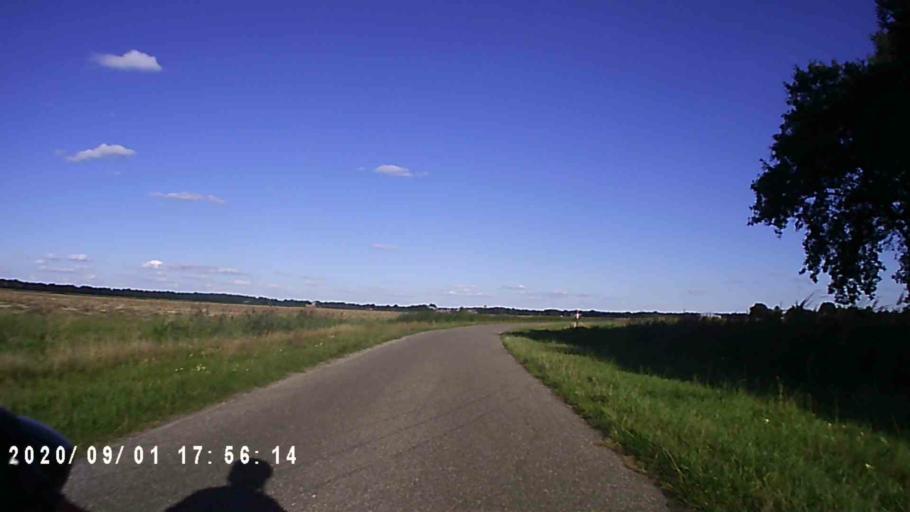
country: NL
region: Groningen
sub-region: Gemeente Slochteren
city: Slochteren
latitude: 53.2095
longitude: 6.7631
